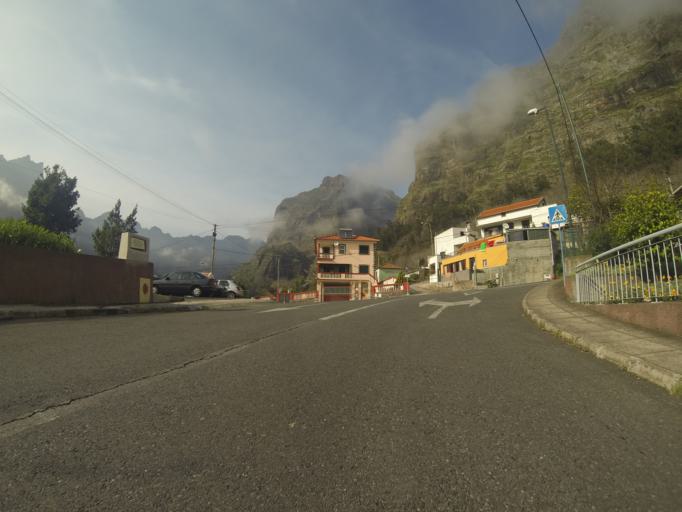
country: PT
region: Madeira
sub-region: Camara de Lobos
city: Curral das Freiras
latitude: 32.7218
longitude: -16.9643
